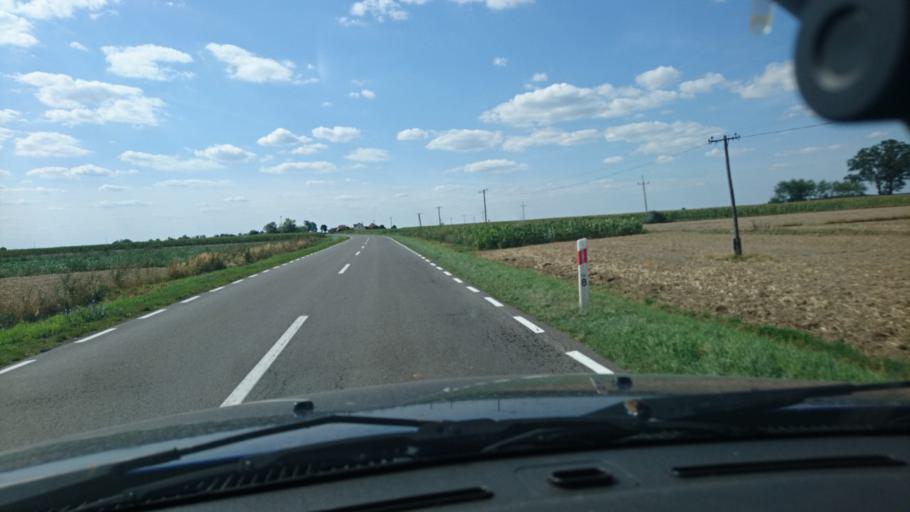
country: PL
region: Greater Poland Voivodeship
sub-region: Powiat krotoszynski
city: Sulmierzyce
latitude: 51.6047
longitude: 17.5636
